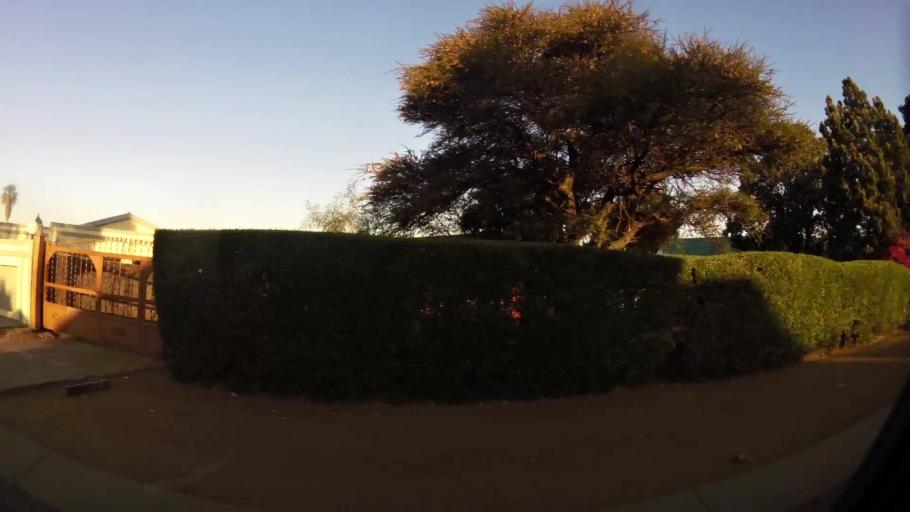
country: ZA
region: North-West
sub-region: Bojanala Platinum District Municipality
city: Rustenburg
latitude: -25.6369
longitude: 27.2058
